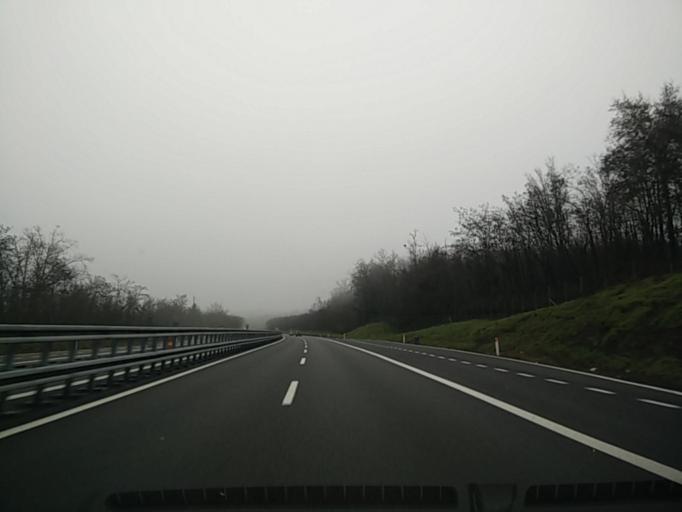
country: IT
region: Piedmont
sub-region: Provincia di Asti
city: Refrancore
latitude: 44.9065
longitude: 8.3379
